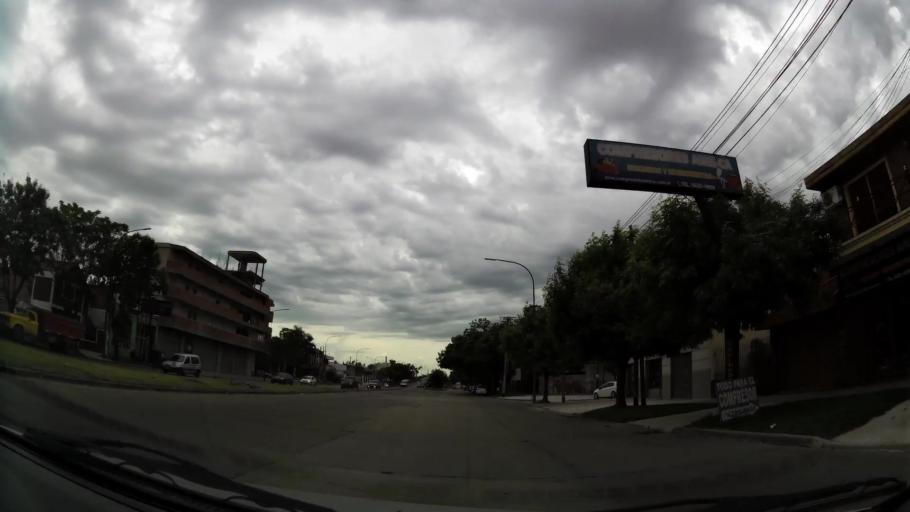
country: AR
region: Buenos Aires
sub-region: Partido de Lanus
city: Lanus
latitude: -34.6899
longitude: -58.3927
